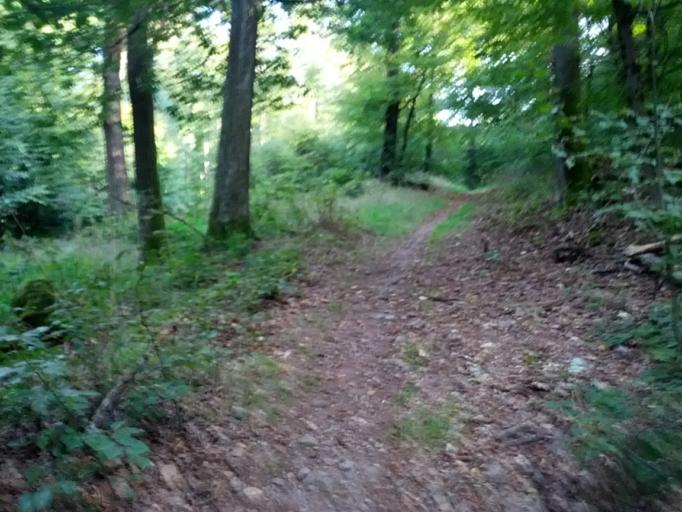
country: DE
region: Thuringia
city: Eisenach
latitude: 50.9473
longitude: 10.3336
